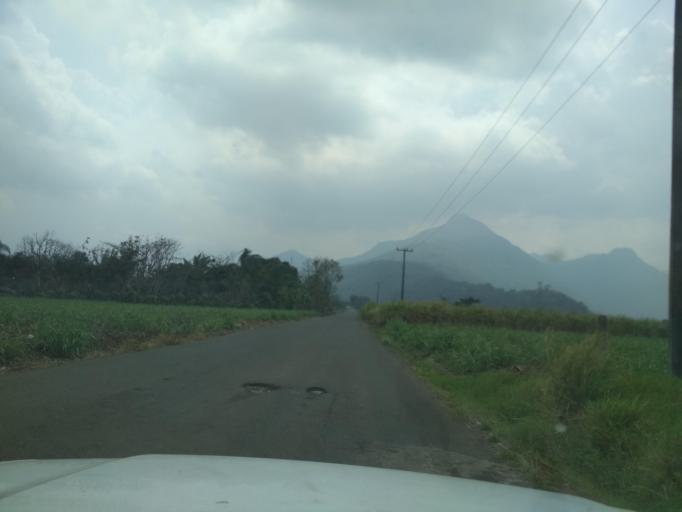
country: MX
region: Veracruz
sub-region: Cordoba
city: San Jose de Tapia
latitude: 18.8419
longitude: -96.9790
